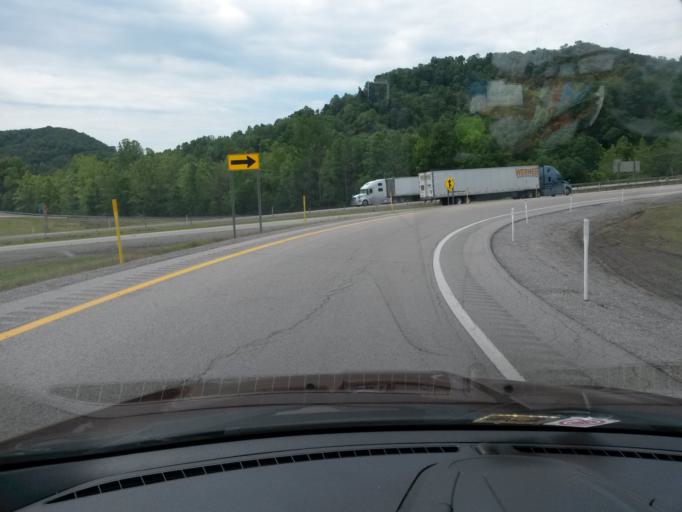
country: US
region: West Virginia
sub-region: Lewis County
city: Weston
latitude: 39.0150
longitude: -80.4691
